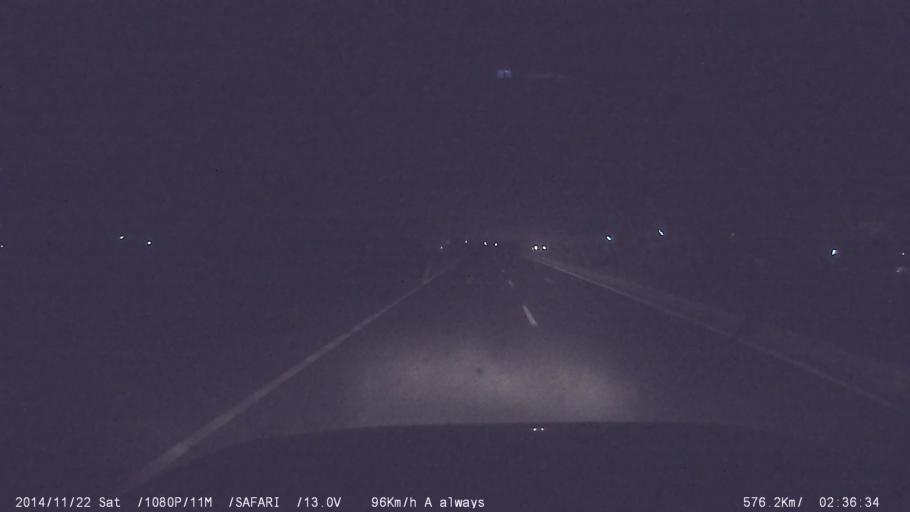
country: IN
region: Tamil Nadu
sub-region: Salem
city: Belur
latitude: 11.6540
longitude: 78.3761
